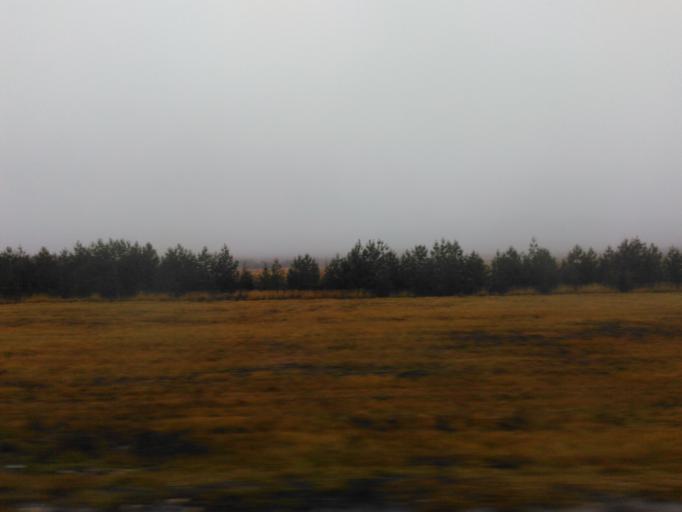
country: RU
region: Tatarstan
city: Sviyazhsk
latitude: 55.7353
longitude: 48.7798
